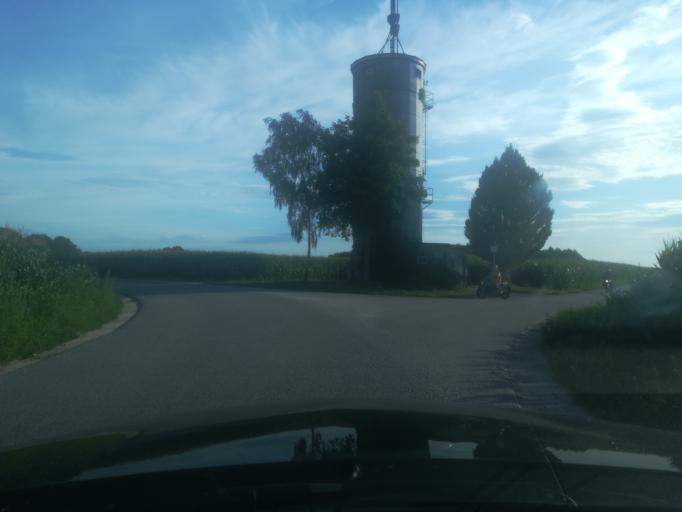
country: AT
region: Upper Austria
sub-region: Wels-Land
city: Marchtrenk
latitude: 48.1574
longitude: 14.1697
